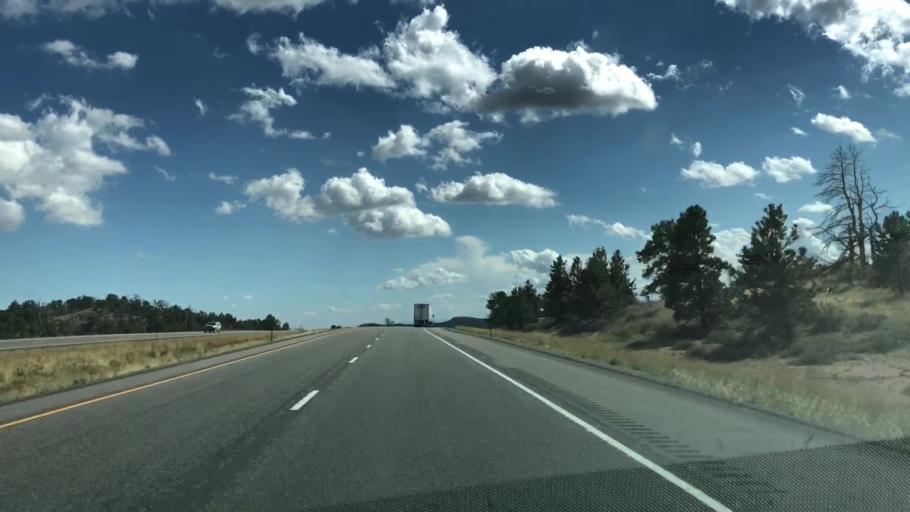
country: US
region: Wyoming
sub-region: Albany County
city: Laramie
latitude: 41.0148
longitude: -105.4203
